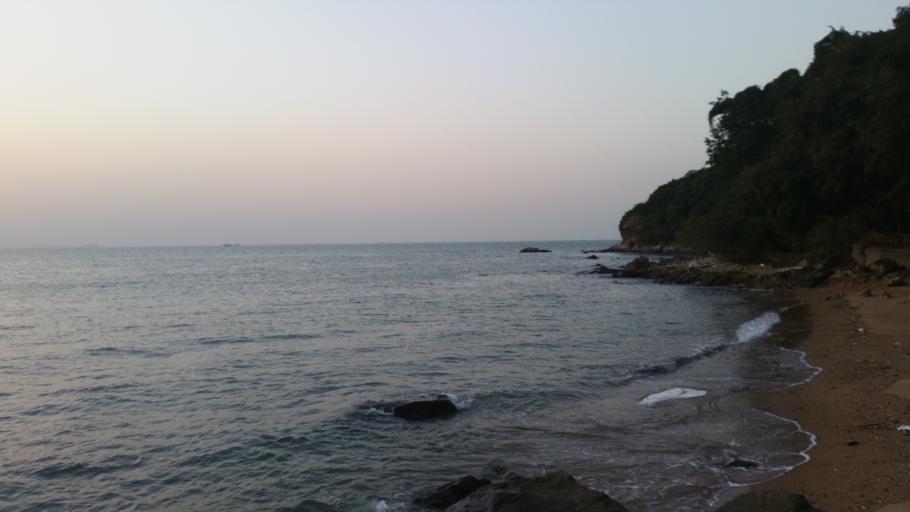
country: HK
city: Tai O
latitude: 22.2529
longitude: 113.8532
